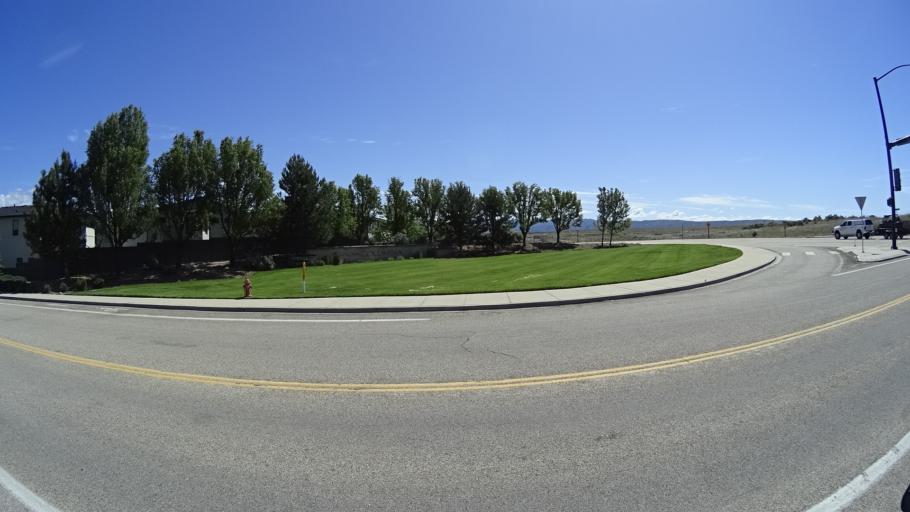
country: US
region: Idaho
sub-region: Ada County
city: Boise
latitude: 43.5408
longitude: -116.1482
